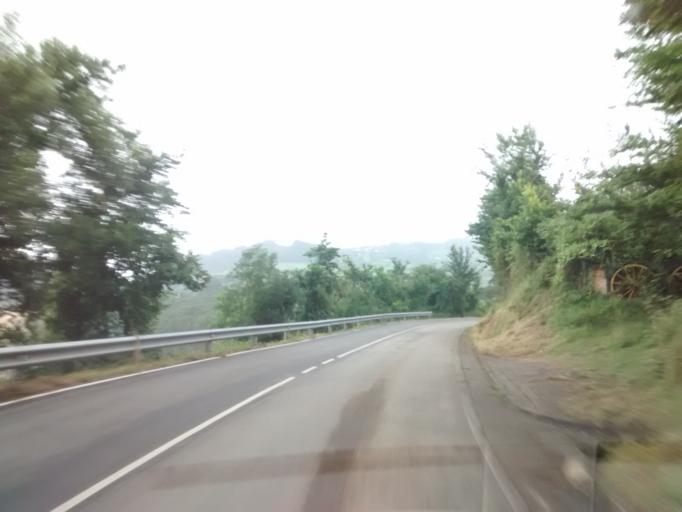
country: ES
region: Asturias
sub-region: Province of Asturias
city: Villaviciosa
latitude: 43.5313
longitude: -5.3912
